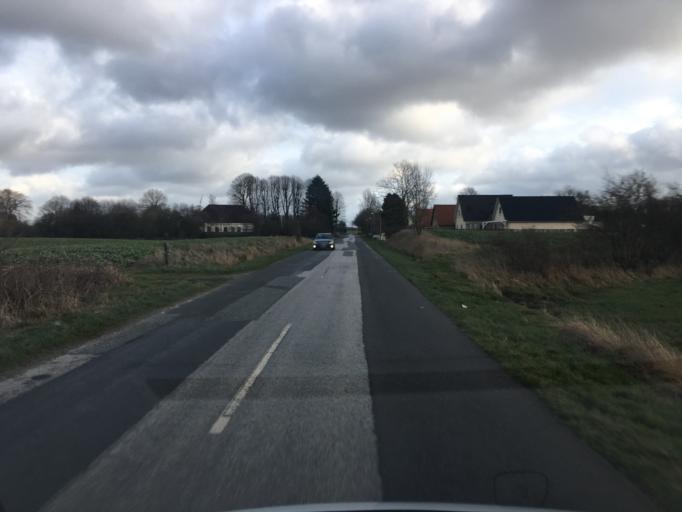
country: DE
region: Schleswig-Holstein
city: Wees
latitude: 54.8957
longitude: 9.4854
